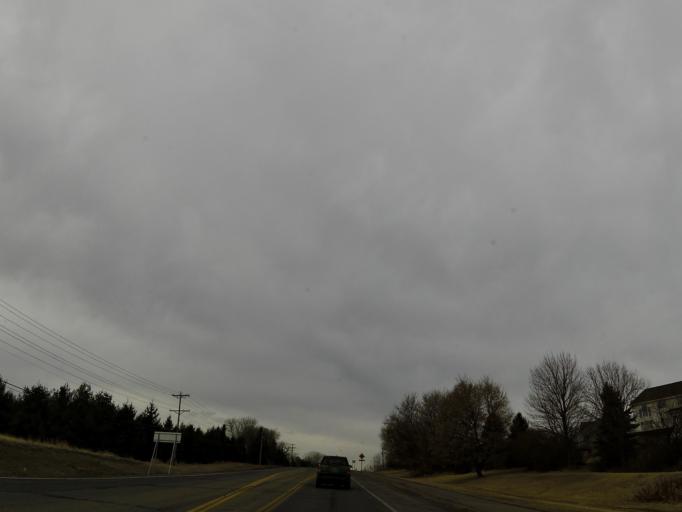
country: US
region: Minnesota
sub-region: Washington County
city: Saint Paul Park
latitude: 44.8479
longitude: -92.9691
